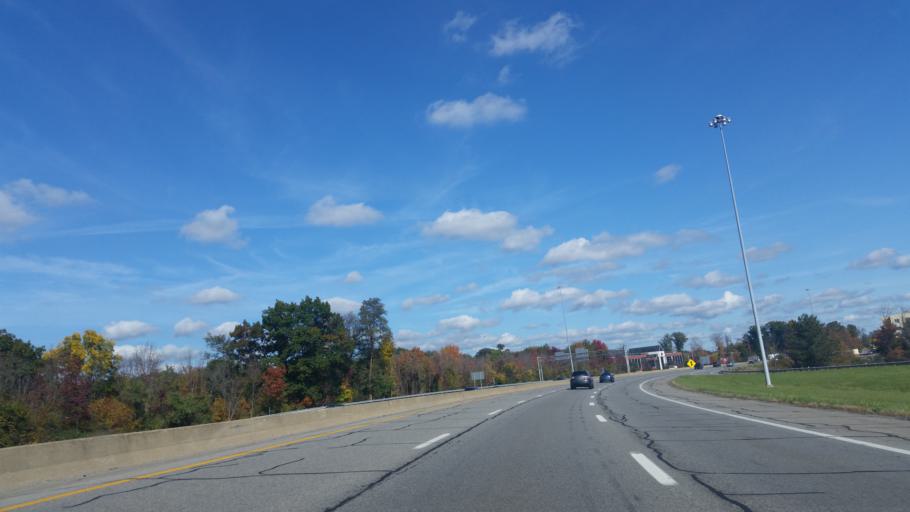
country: US
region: Ohio
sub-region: Summit County
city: Montrose-Ghent
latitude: 41.1390
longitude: -81.6496
